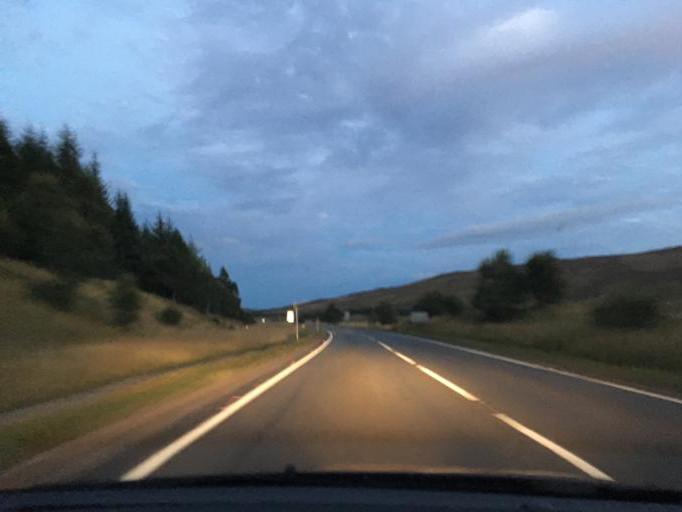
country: GB
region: Scotland
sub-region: Perth and Kinross
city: Aberfeldy
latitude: 56.8050
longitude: -4.0682
